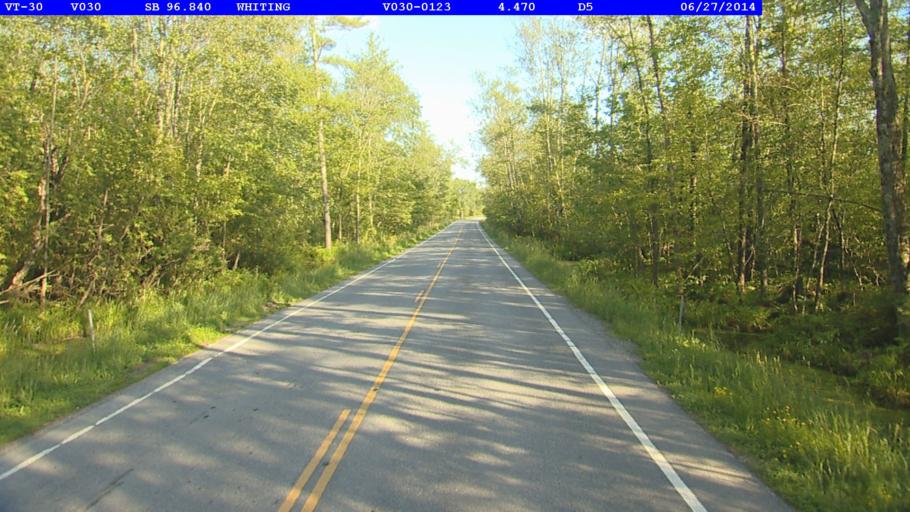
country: US
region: Vermont
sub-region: Addison County
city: Middlebury (village)
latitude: 43.9014
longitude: -73.2060
